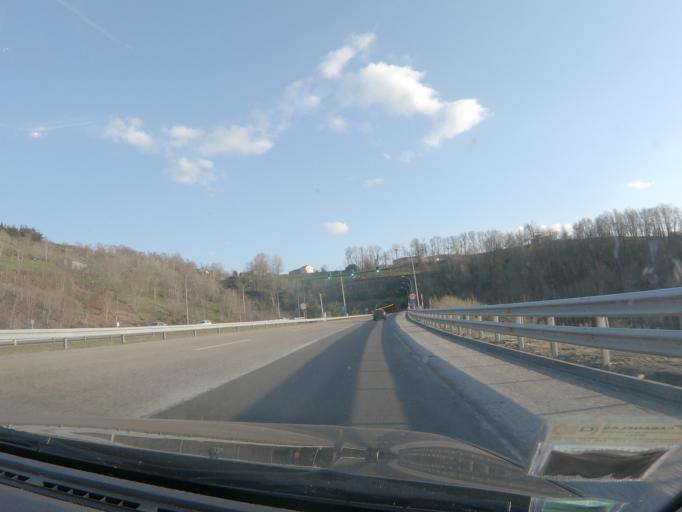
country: ES
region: Castille and Leon
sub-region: Provincia de Leon
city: Balboa
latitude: 42.7380
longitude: -7.0472
